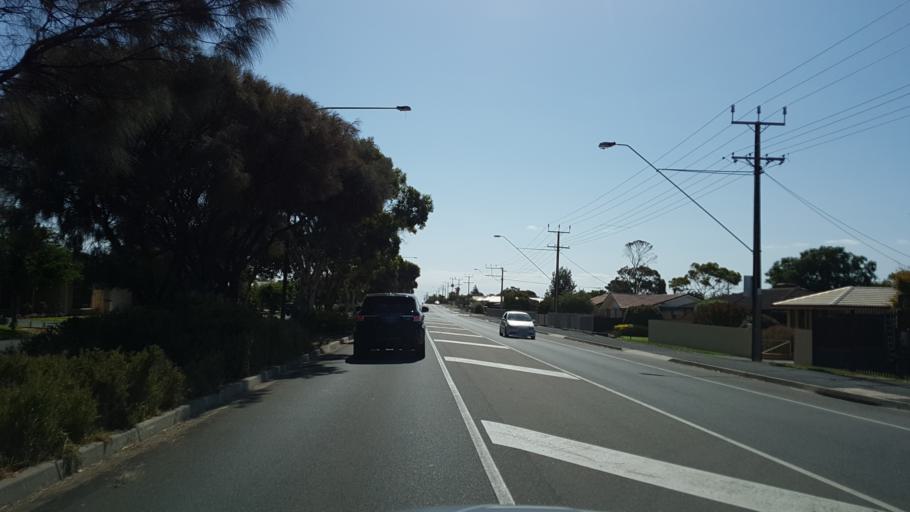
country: AU
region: South Australia
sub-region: Onkaparinga
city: Port Willunga
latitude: -35.2789
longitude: 138.4515
